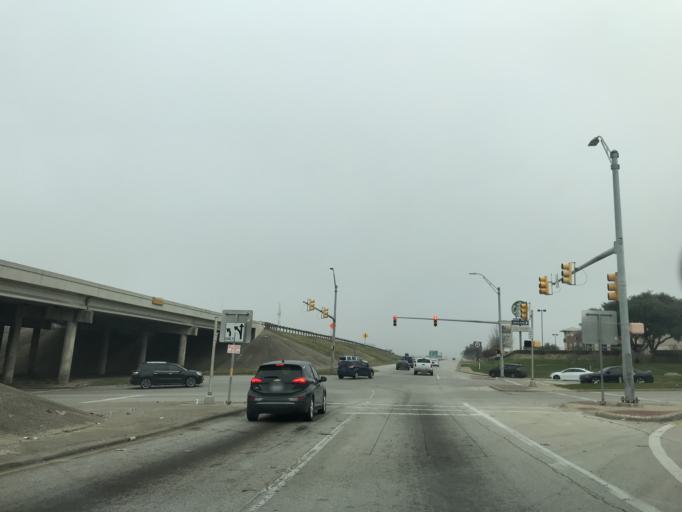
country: US
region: Texas
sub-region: Tarrant County
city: Euless
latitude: 32.8219
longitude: -97.0607
